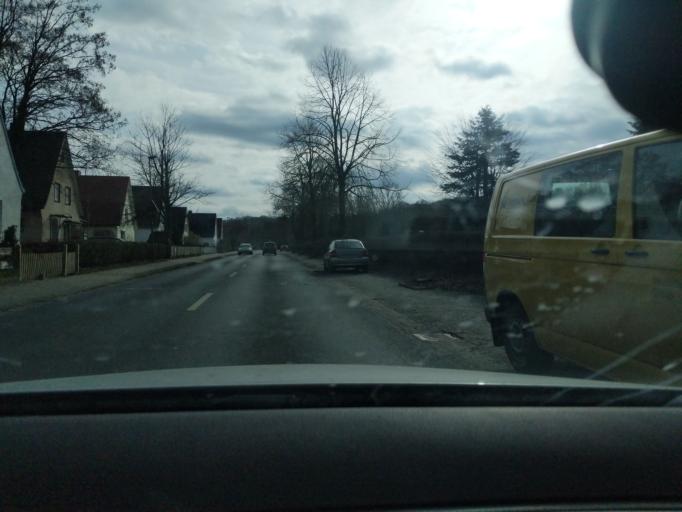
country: DE
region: Lower Saxony
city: Himmelpforten
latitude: 53.6145
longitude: 9.3134
